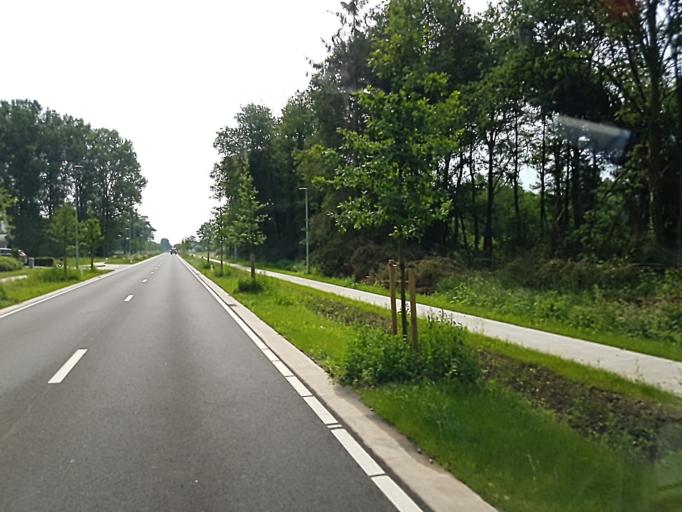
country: BE
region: Flanders
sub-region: Provincie Limburg
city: Leopoldsburg
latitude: 51.1389
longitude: 5.2303
